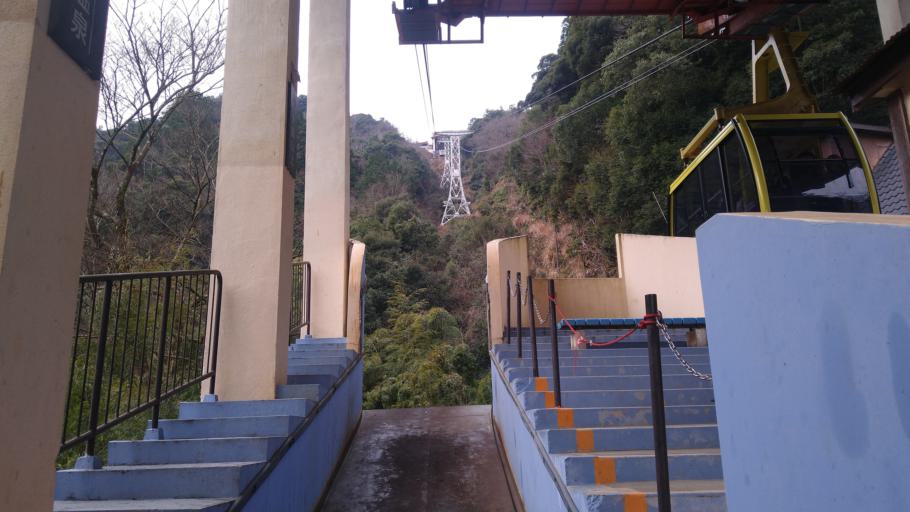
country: JP
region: Hyogo
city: Toyooka
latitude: 35.6239
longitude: 134.8004
